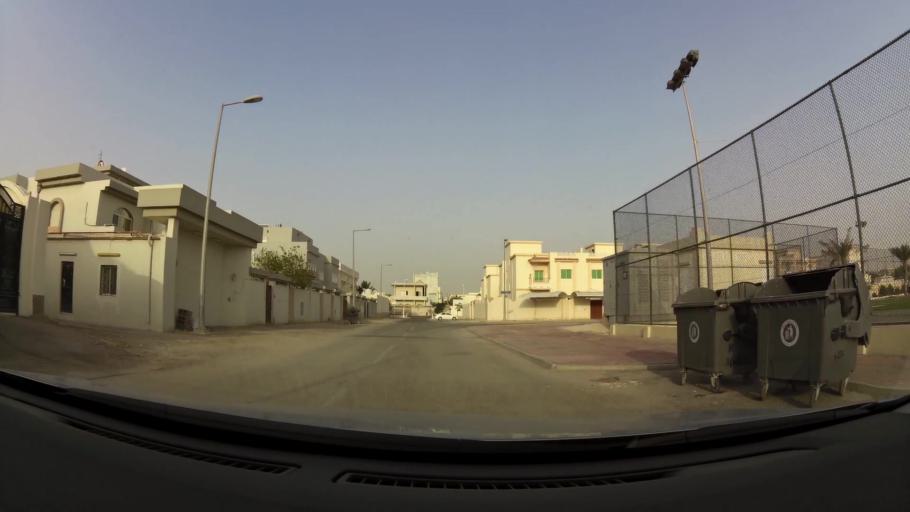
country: QA
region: Baladiyat ar Rayyan
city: Ar Rayyan
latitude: 25.2495
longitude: 51.4474
